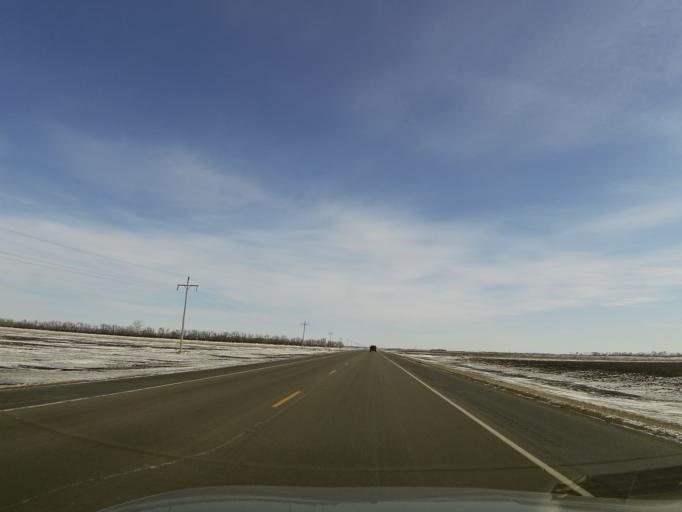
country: US
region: North Dakota
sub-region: Walsh County
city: Grafton
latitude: 48.4124
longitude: -97.3242
